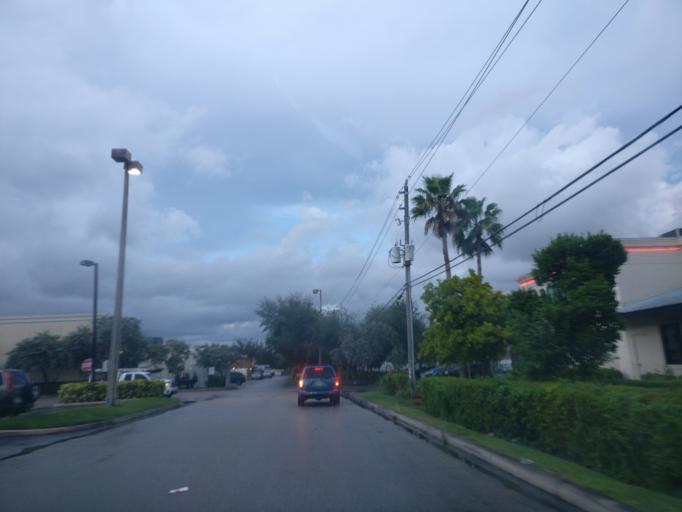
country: US
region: Florida
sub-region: Palm Beach County
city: Plantation Mobile Home Park
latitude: 26.7084
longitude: -80.1497
